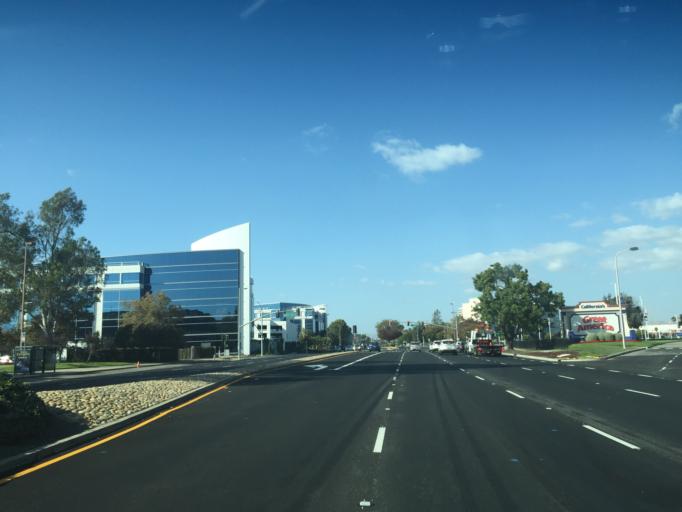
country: US
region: California
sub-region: Santa Clara County
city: Santa Clara
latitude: 37.3987
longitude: -121.9779
